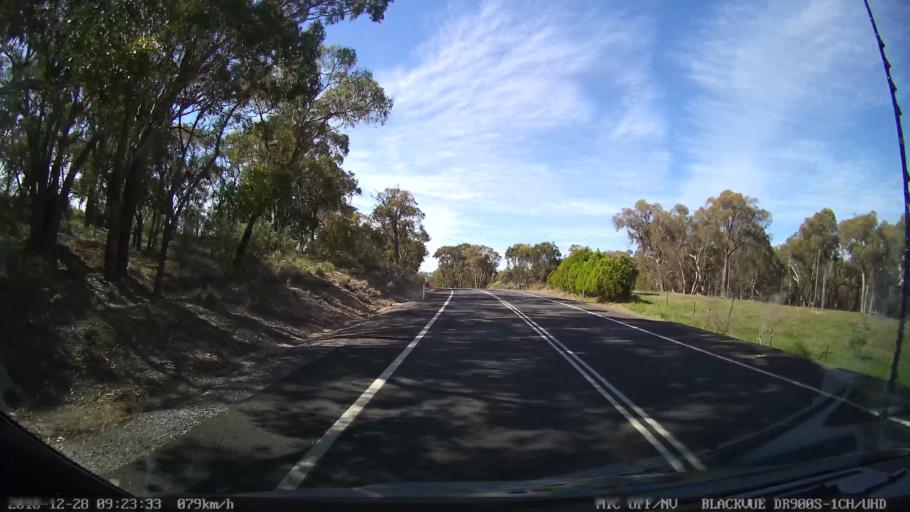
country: AU
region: New South Wales
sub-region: Upper Lachlan Shire
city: Crookwell
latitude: -34.3868
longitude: 149.3841
